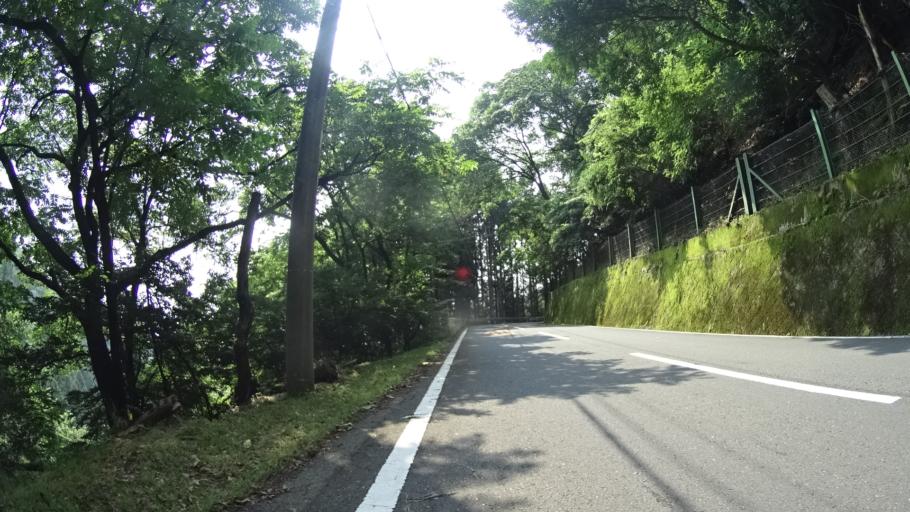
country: JP
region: Gunma
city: Tomioka
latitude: 36.0609
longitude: 138.8481
